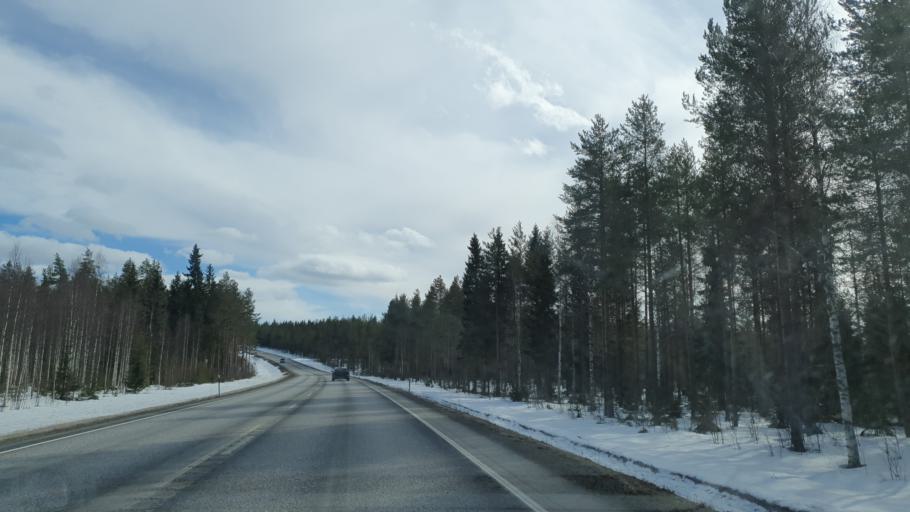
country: FI
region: Kainuu
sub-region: Kajaani
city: Paltamo
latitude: 64.3742
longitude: 28.0283
